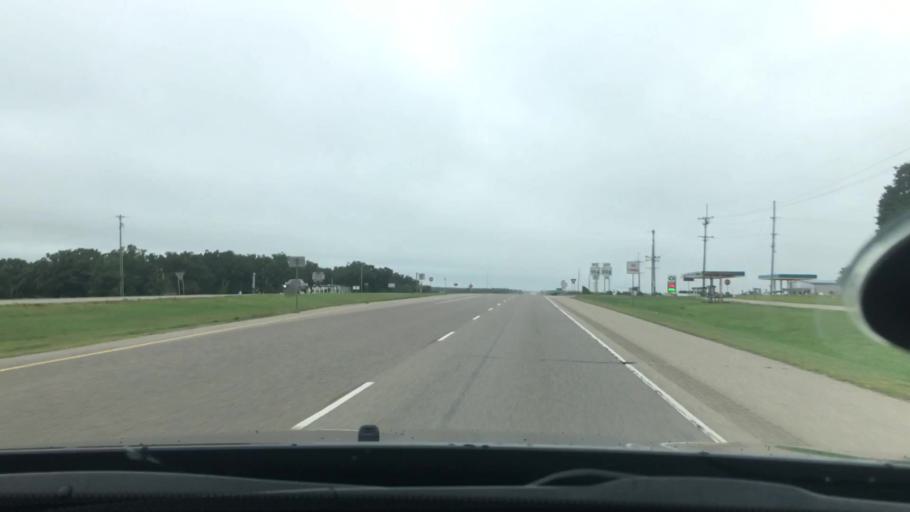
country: US
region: Oklahoma
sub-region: Seminole County
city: Seminole
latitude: 35.3469
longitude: -96.6715
